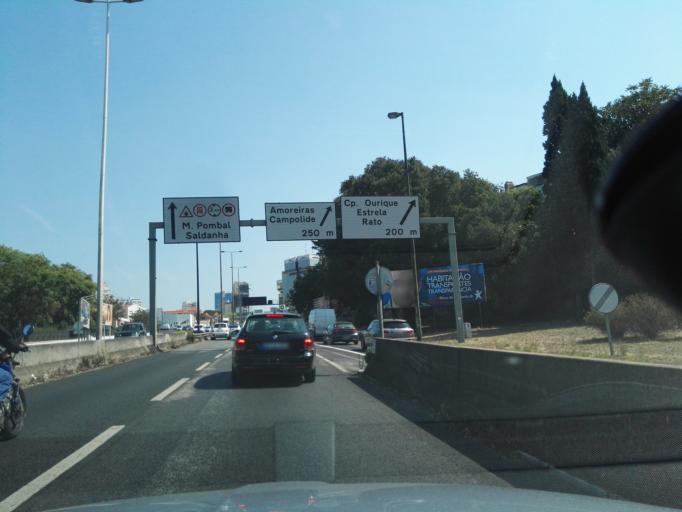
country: PT
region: Lisbon
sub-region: Lisbon
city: Lisbon
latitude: 38.7224
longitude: -9.1700
